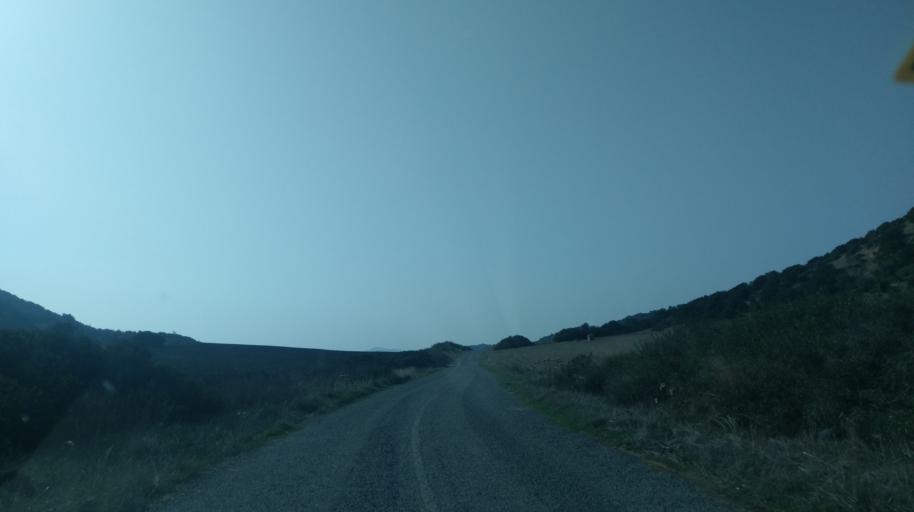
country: CY
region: Ammochostos
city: Rizokarpaso
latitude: 35.5520
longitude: 34.3606
